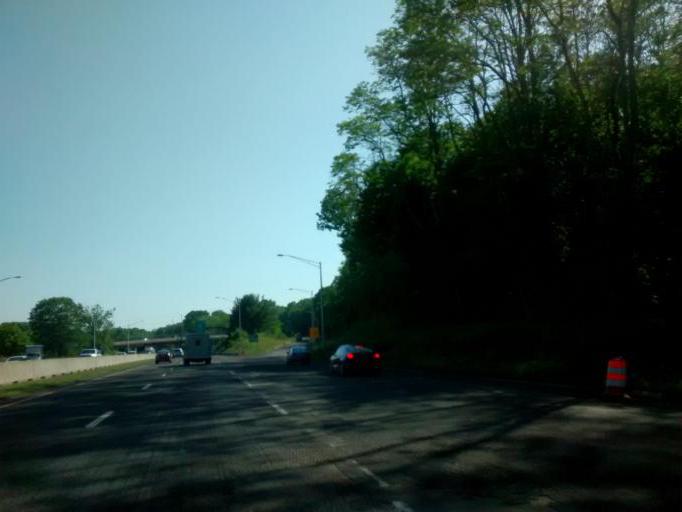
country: US
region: Connecticut
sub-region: New London County
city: Niantic
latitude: 41.3720
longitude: -72.1993
